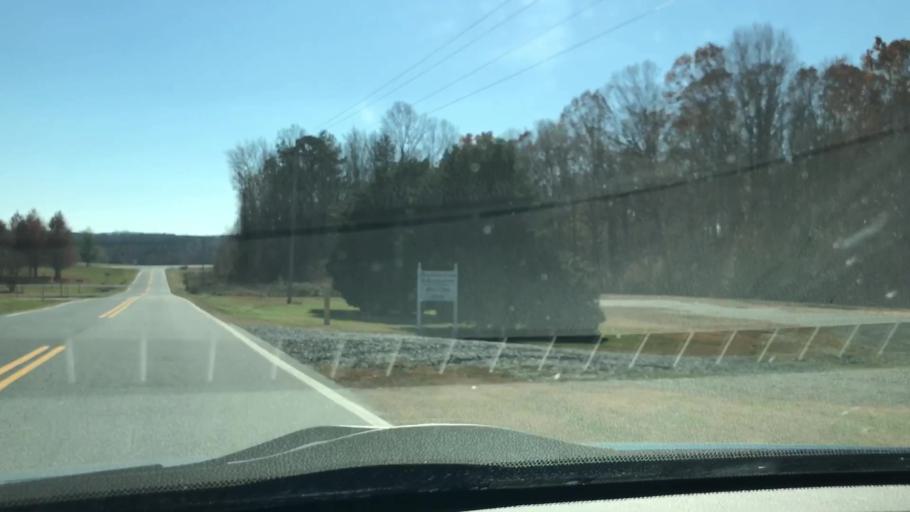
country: US
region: North Carolina
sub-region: Davidson County
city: Denton
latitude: 35.6423
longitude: -79.9728
